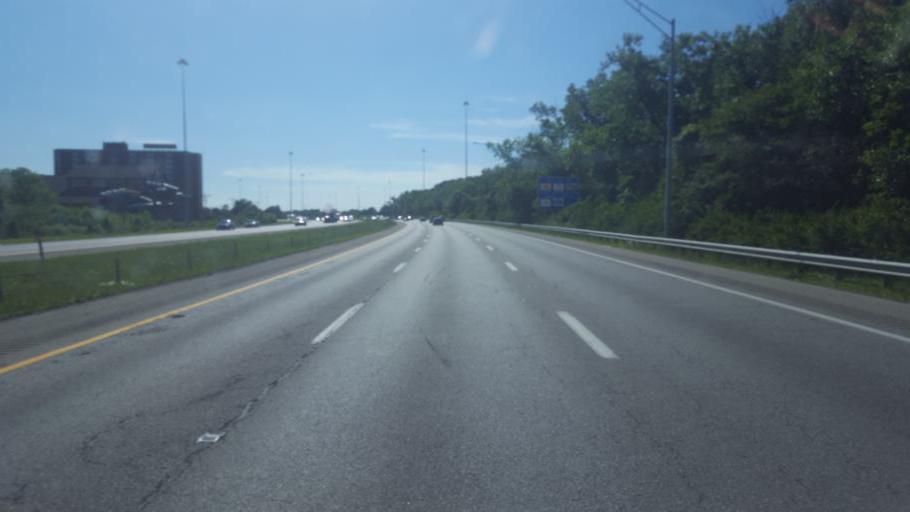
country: US
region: Ohio
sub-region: Franklin County
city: Blacklick Estates
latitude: 39.9367
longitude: -82.8688
